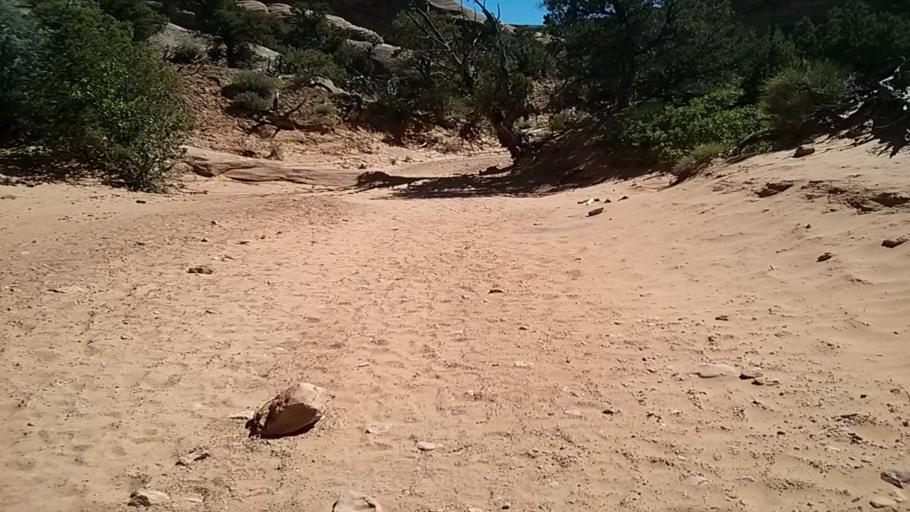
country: US
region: Utah
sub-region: Grand County
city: Moab
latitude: 38.8024
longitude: -109.6106
